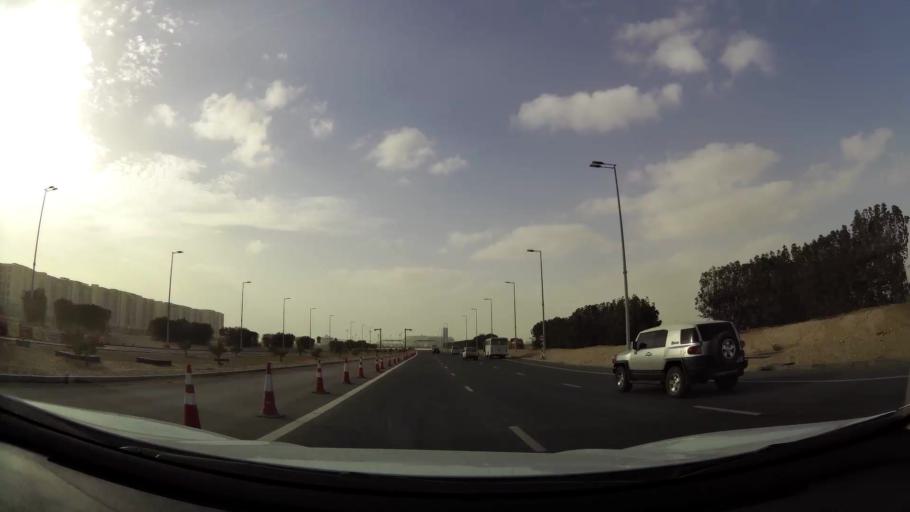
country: AE
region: Abu Dhabi
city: Abu Dhabi
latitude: 24.4586
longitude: 54.6193
